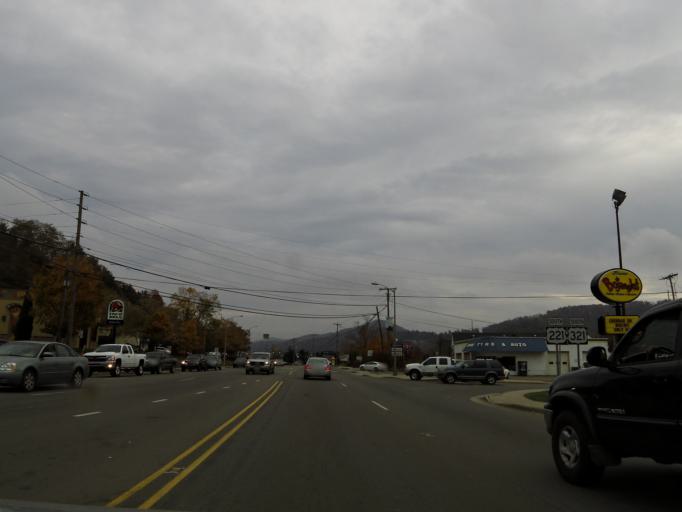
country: US
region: North Carolina
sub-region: Watauga County
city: Boone
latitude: 36.2050
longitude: -81.6688
